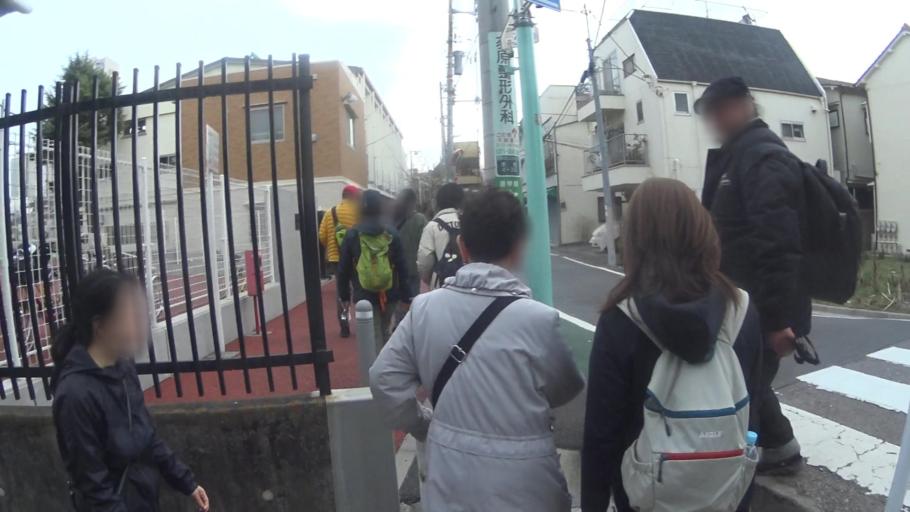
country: JP
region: Tokyo
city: Tokyo
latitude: 35.6849
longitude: 139.6791
